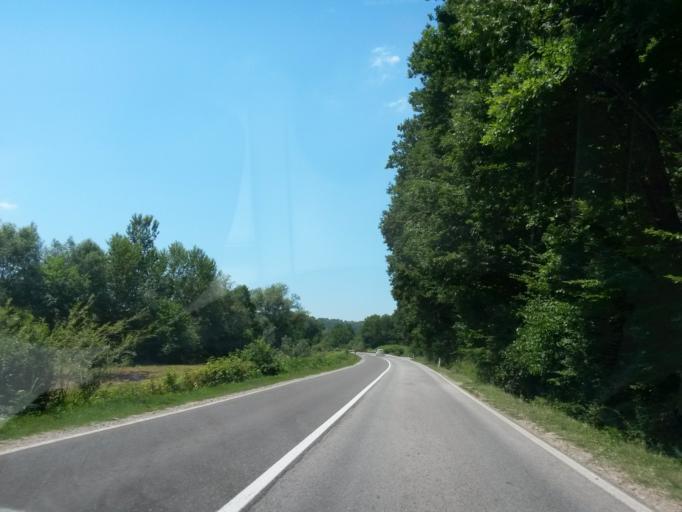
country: BA
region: Republika Srpska
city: Doboj
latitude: 44.8644
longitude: 18.0693
